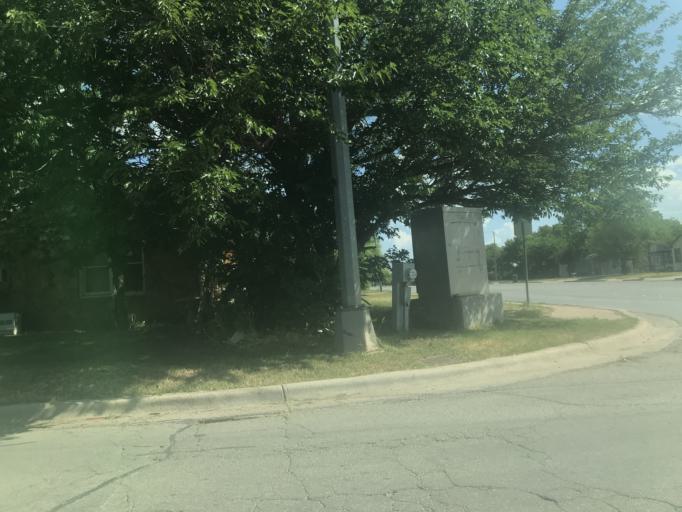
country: US
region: Texas
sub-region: Taylor County
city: Abilene
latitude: 32.4375
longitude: -99.7592
